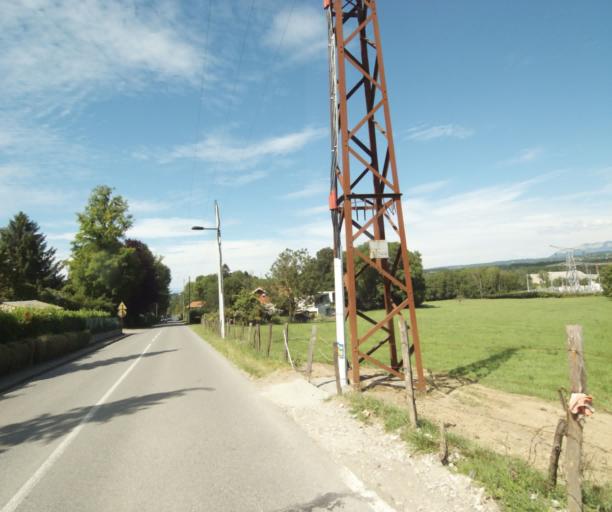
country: FR
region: Rhone-Alpes
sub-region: Departement de la Haute-Savoie
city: Allinges
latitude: 46.3295
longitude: 6.4742
